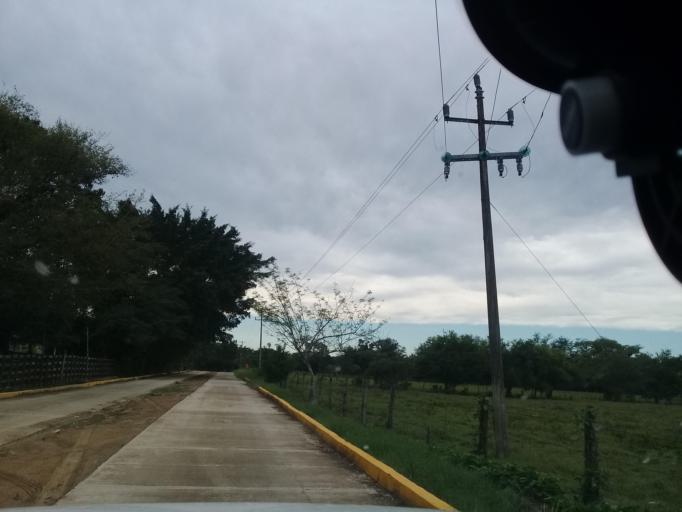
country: MX
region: Hidalgo
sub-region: Huejutla de Reyes
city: Chalahuiyapa
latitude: 21.1627
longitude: -98.3558
